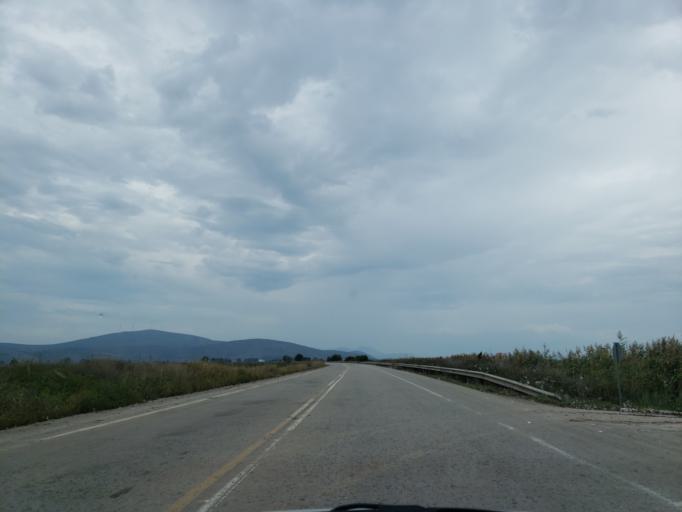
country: GR
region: Central Greece
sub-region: Nomos Voiotias
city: Orchomenos
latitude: 38.4930
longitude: 23.0172
